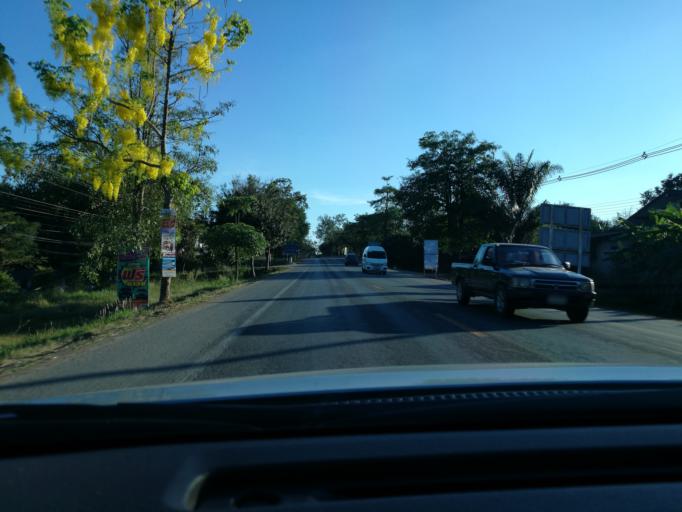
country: TH
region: Phitsanulok
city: Nakhon Thai
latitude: 17.0598
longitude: 100.8097
